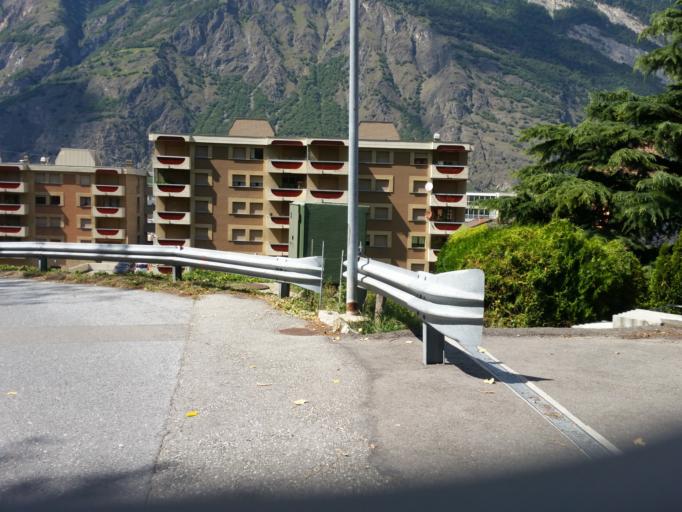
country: CH
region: Valais
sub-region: Martigny District
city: Saxon
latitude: 46.1479
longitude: 7.1753
